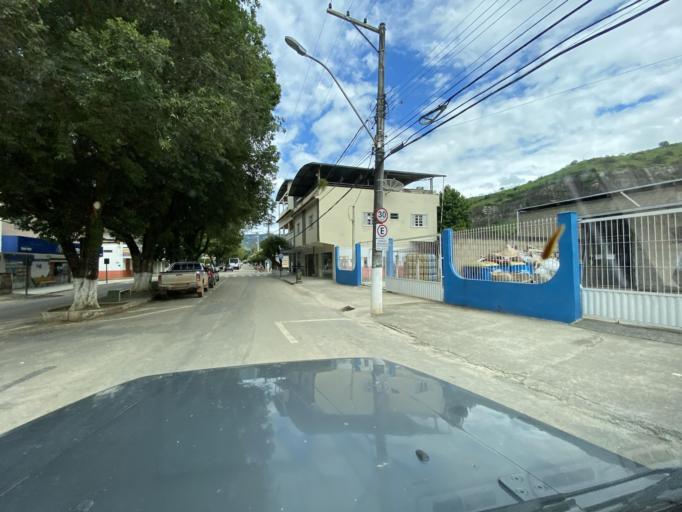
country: BR
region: Espirito Santo
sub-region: Jeronimo Monteiro
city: Jeronimo Monteiro
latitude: -20.7885
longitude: -41.3909
